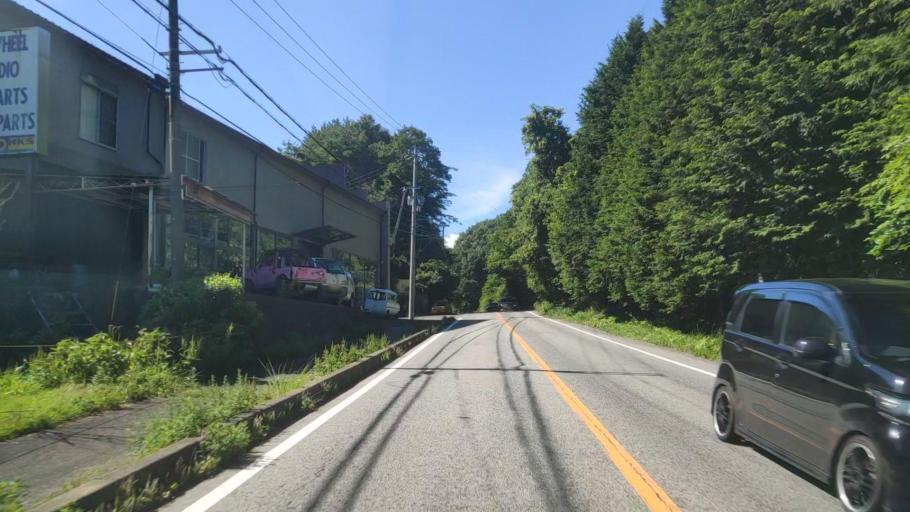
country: JP
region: Nara
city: Haibara-akanedai
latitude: 34.5884
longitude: 135.9641
